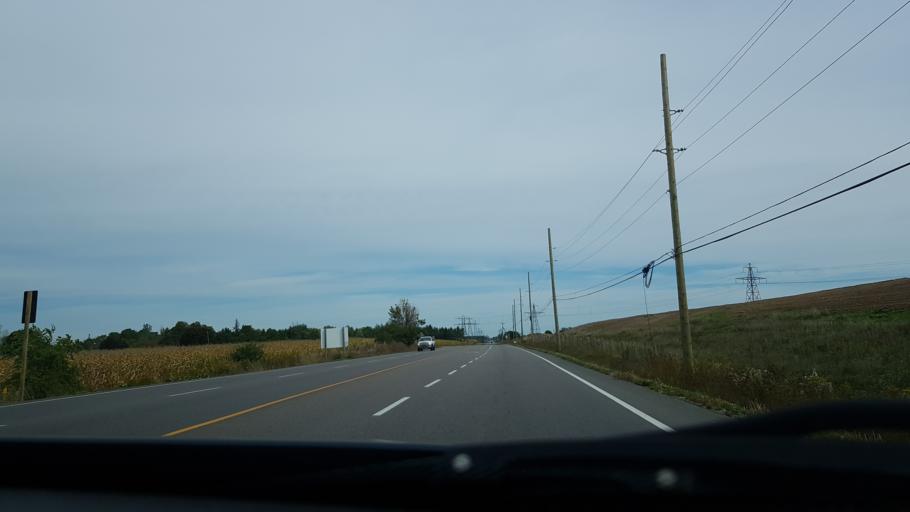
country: CA
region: Ontario
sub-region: Wellington County
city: Guelph
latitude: 43.4750
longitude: -80.3026
